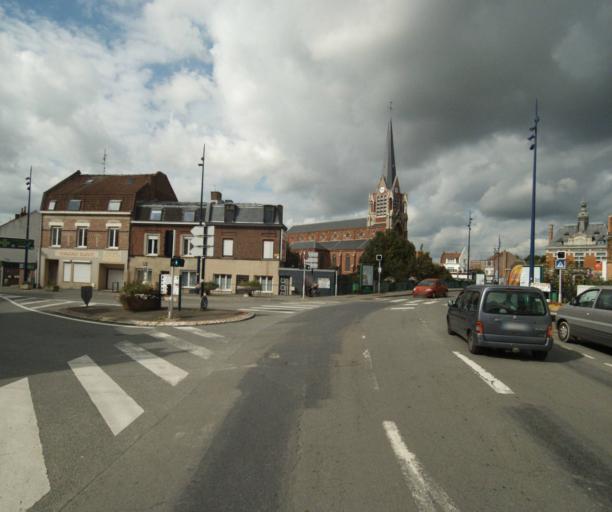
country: FR
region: Nord-Pas-de-Calais
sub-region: Departement du Nord
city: Perenchies
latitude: 50.6674
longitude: 2.9734
